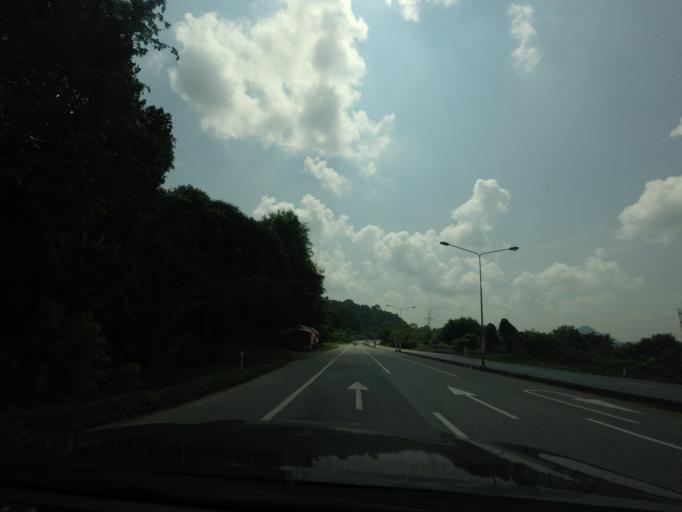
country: TH
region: Uttaradit
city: Lap Lae
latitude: 17.7878
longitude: 100.1179
